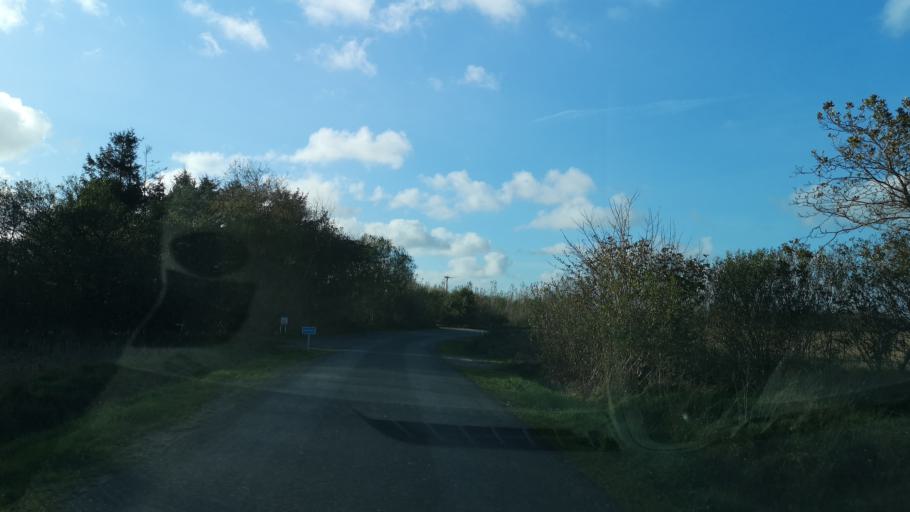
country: DK
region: Central Jutland
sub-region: Ringkobing-Skjern Kommune
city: Skjern
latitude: 55.8572
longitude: 8.3482
